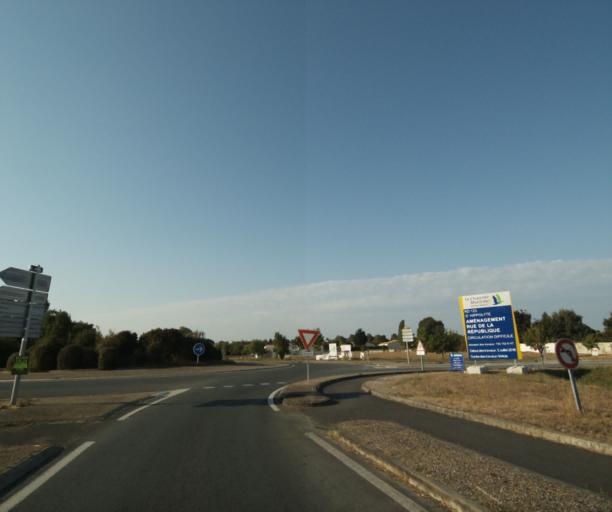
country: FR
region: Poitou-Charentes
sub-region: Departement de la Charente-Maritime
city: Saint-Hippolyte
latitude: 45.9175
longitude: -0.8864
